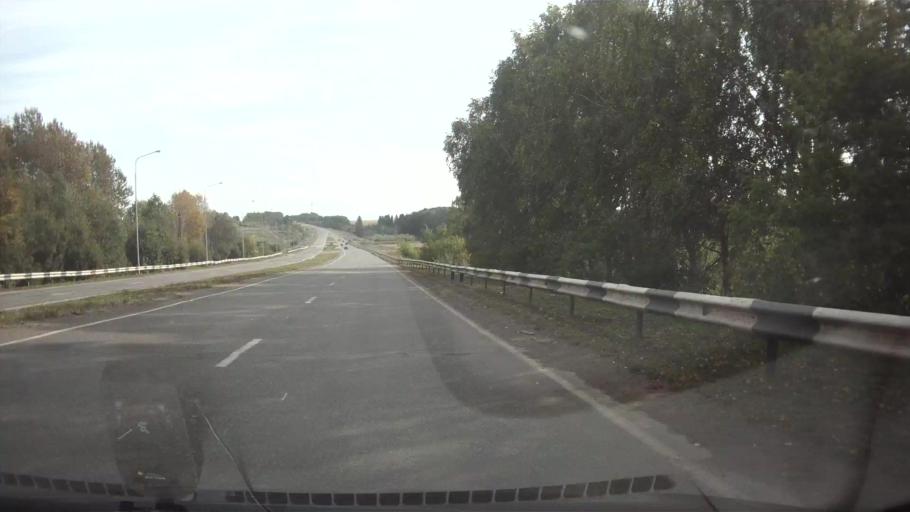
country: RU
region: Mariy-El
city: Sovetskiy
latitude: 56.7518
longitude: 48.4872
